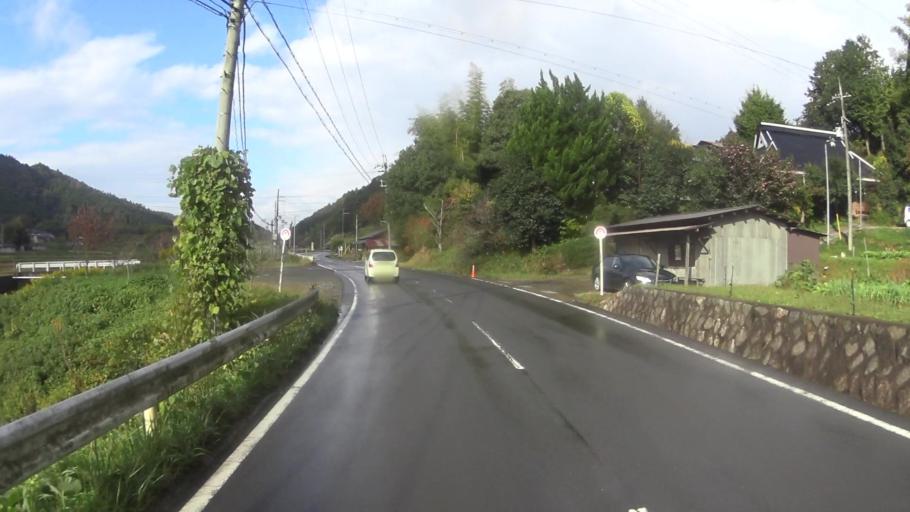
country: JP
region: Kyoto
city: Ayabe
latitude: 35.3686
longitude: 135.1947
